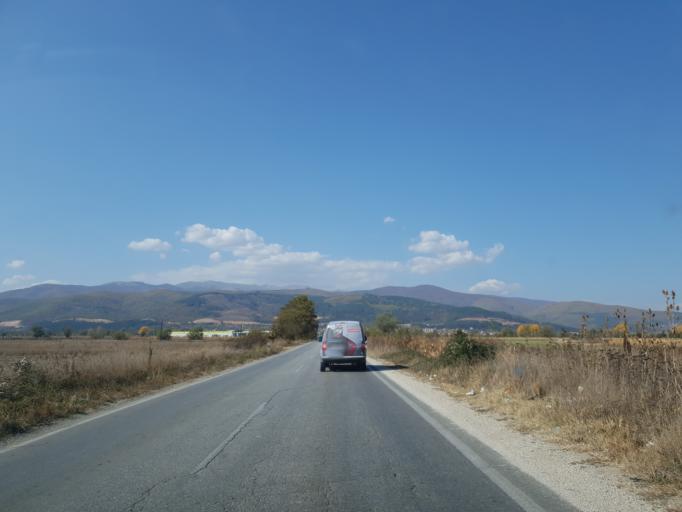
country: MK
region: Kicevo
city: Kicevo
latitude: 41.4875
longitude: 20.9728
